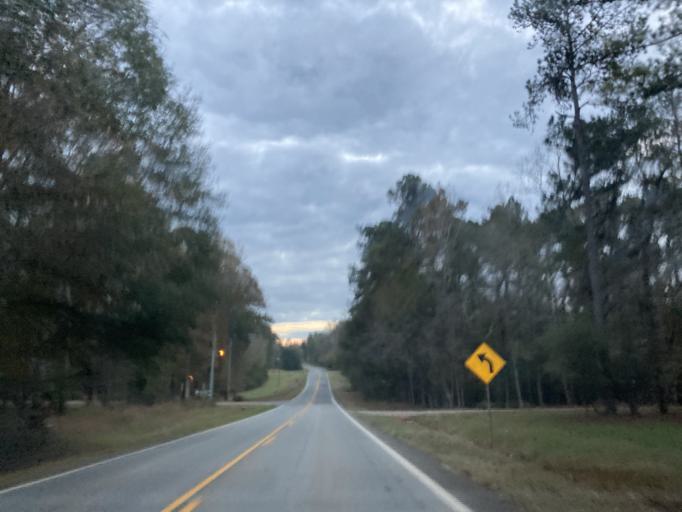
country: US
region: Georgia
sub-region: Jones County
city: Gray
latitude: 32.9768
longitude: -83.5041
